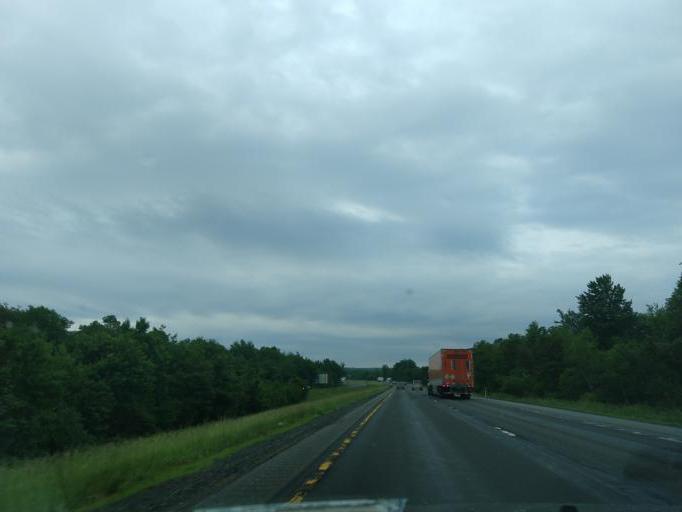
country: US
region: Pennsylvania
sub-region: Schuylkill County
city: McAdoo
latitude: 40.9054
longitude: -76.0264
